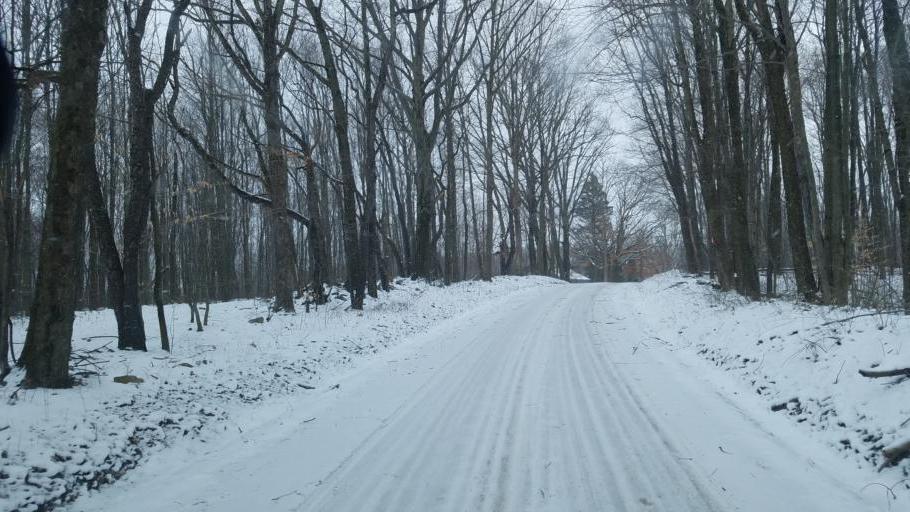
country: US
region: Pennsylvania
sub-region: Crawford County
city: Cochranton
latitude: 41.4458
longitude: -79.9910
